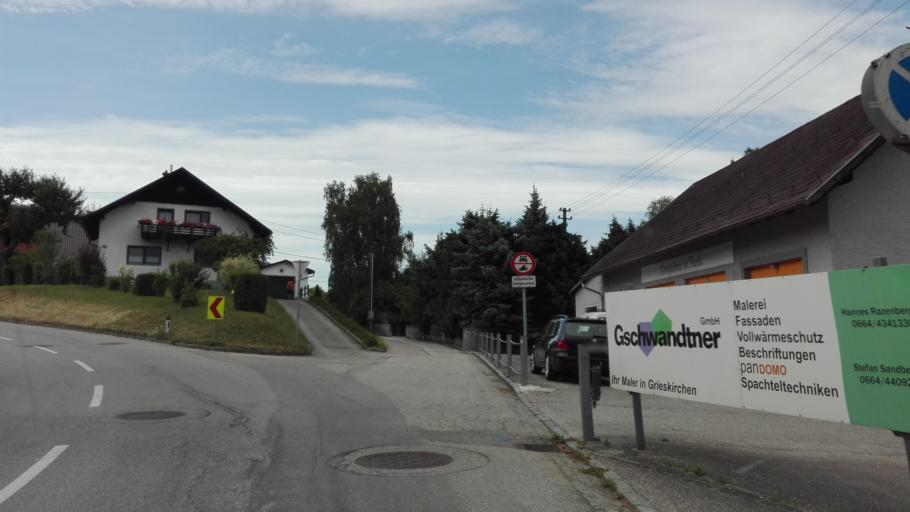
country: AT
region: Upper Austria
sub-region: Politischer Bezirk Grieskirchen
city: Grieskirchen
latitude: 48.2390
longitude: 13.8231
